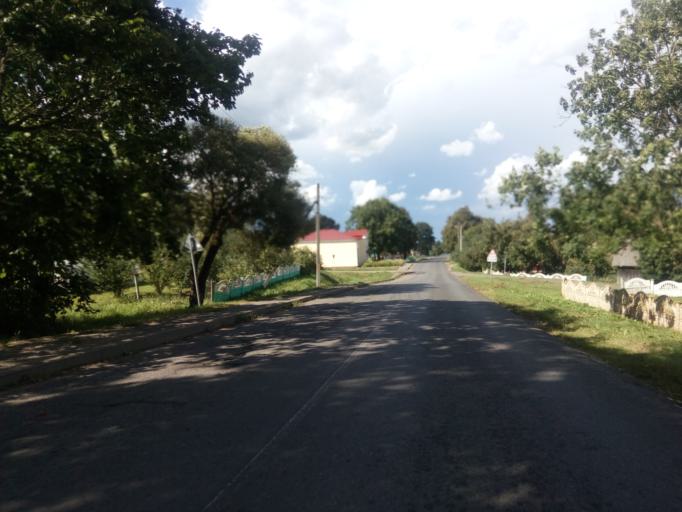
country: BY
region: Vitebsk
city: Dzisna
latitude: 55.7053
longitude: 28.1846
